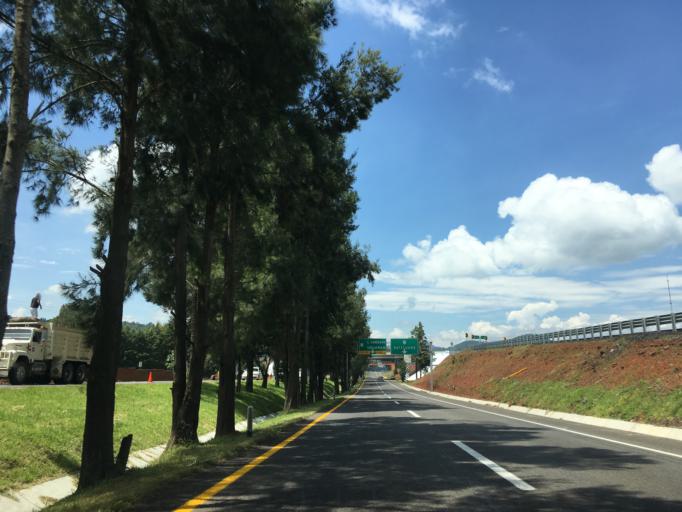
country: MX
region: Michoacan
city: Patzcuaro
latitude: 19.5327
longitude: -101.5534
